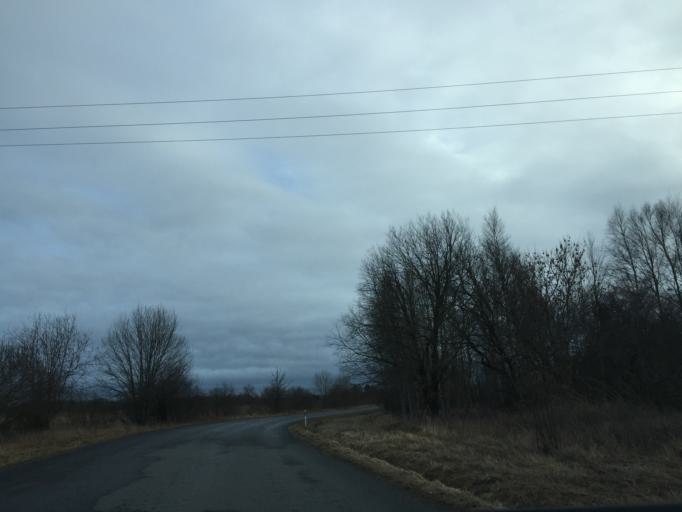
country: EE
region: Laeaene
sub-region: Haapsalu linn
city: Haapsalu
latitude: 58.8127
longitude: 23.5502
